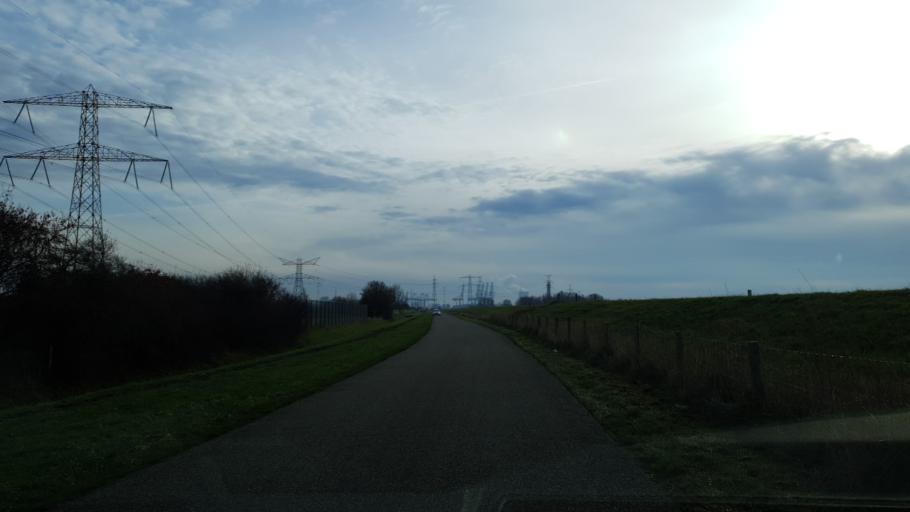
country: NL
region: North Brabant
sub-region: Gemeente Woensdrecht
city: Woensdrecht
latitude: 51.3835
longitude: 4.2446
